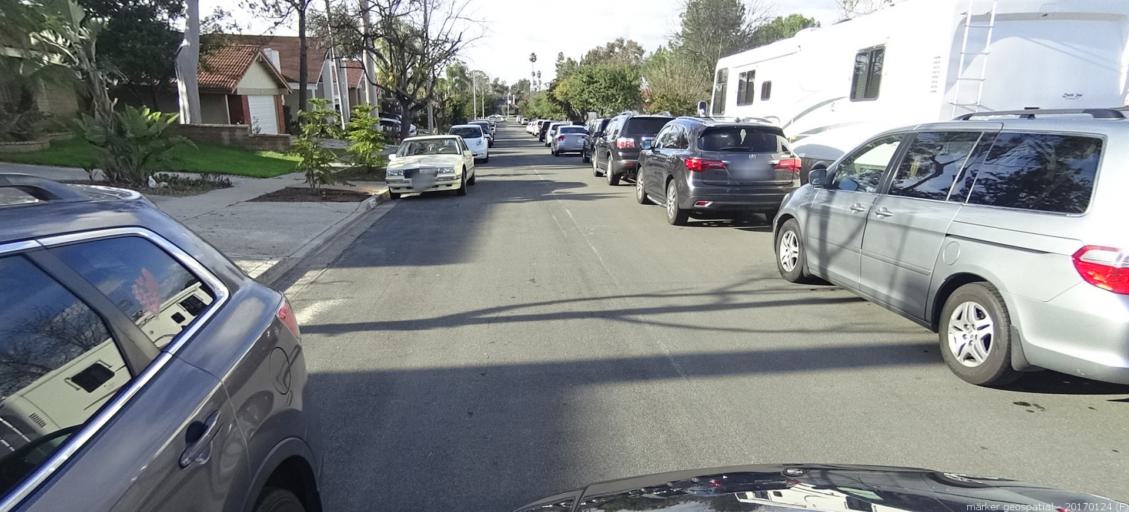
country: US
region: California
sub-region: Orange County
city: Laguna Hills
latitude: 33.6278
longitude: -117.7009
